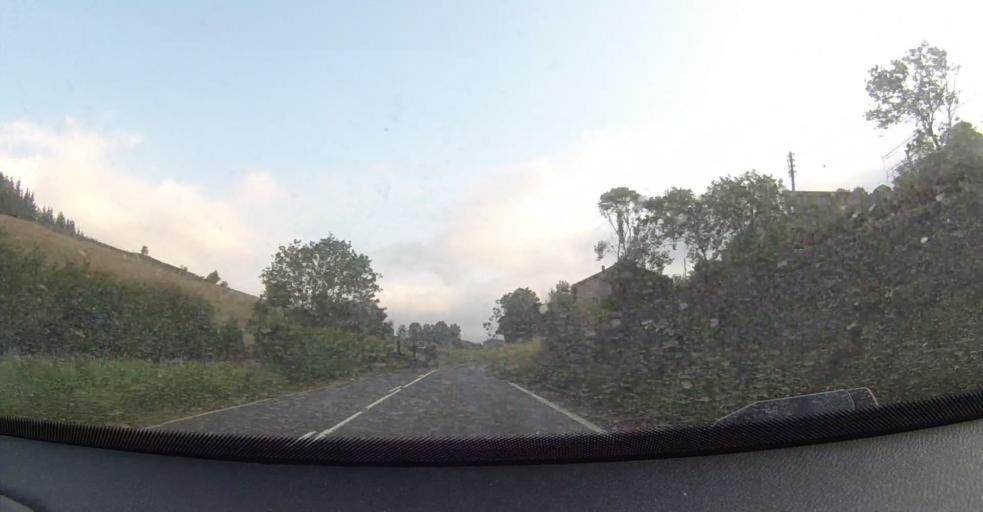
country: ES
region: Basque Country
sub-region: Bizkaia
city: Urrestieta
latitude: 43.2315
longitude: -3.1593
